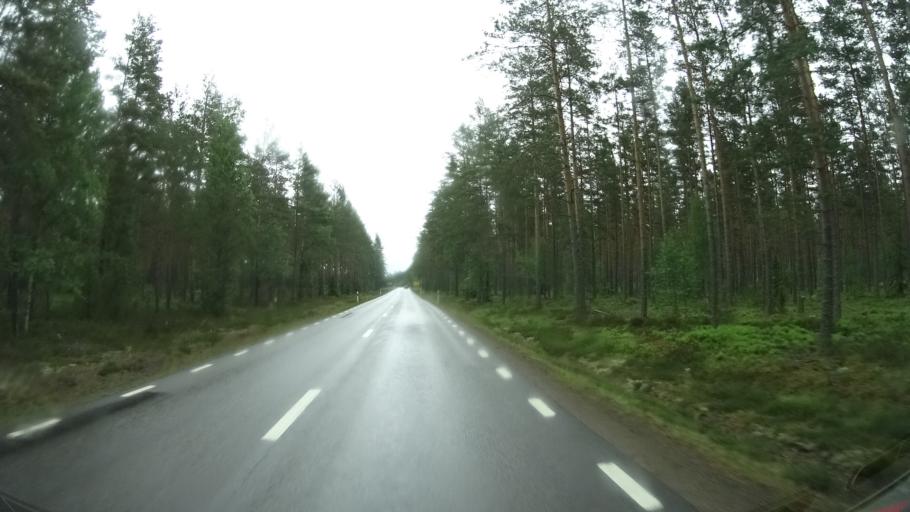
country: SE
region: Kalmar
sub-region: Hultsfreds Kommun
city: Hultsfred
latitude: 57.5152
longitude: 15.8174
